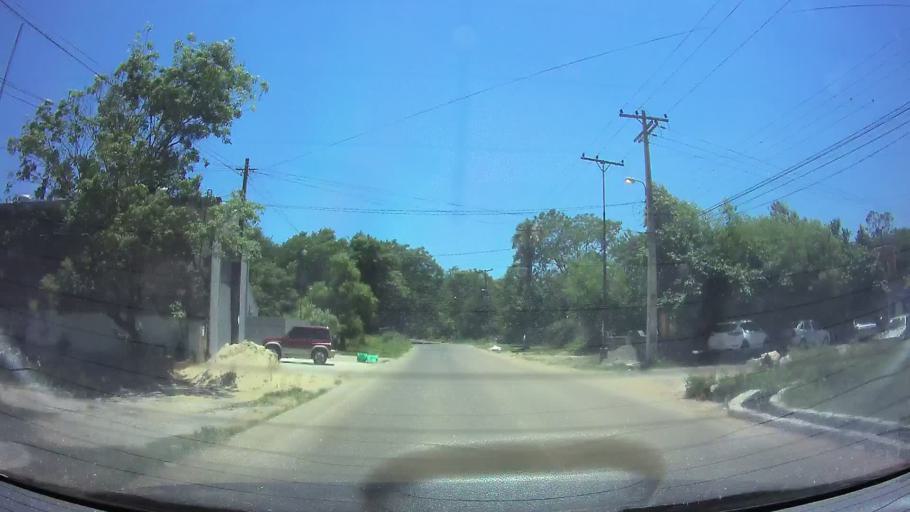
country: PY
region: Central
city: Fernando de la Mora
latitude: -25.2713
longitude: -57.5181
